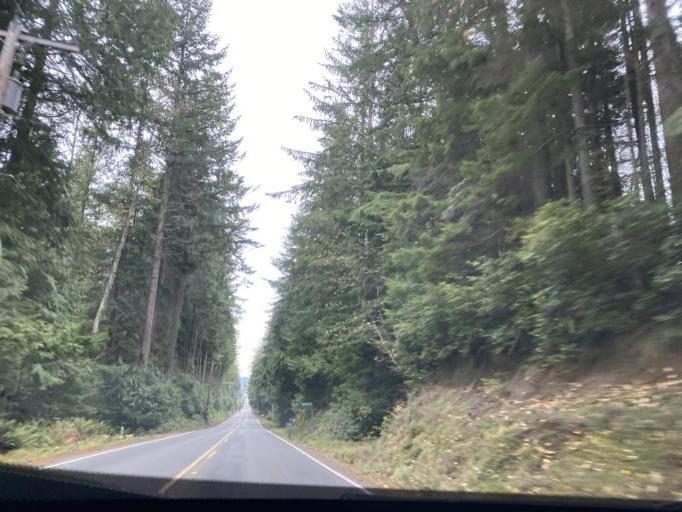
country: US
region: Washington
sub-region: Island County
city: Freeland
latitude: 48.0726
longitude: -122.4850
